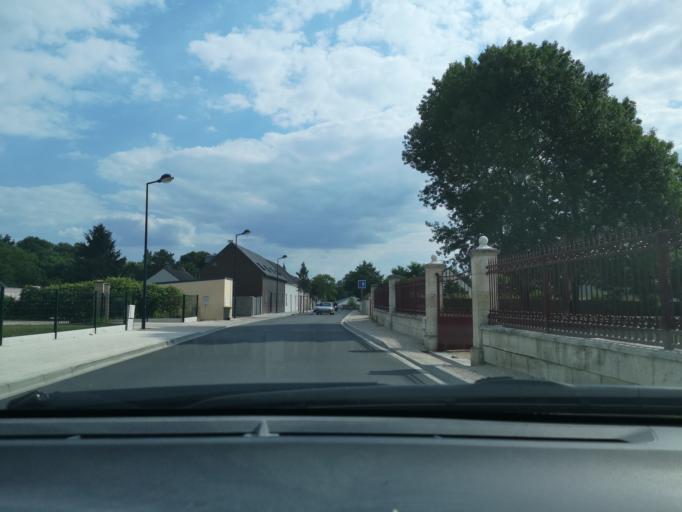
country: FR
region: Centre
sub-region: Departement du Loiret
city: Semoy
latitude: 47.9268
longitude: 1.9589
